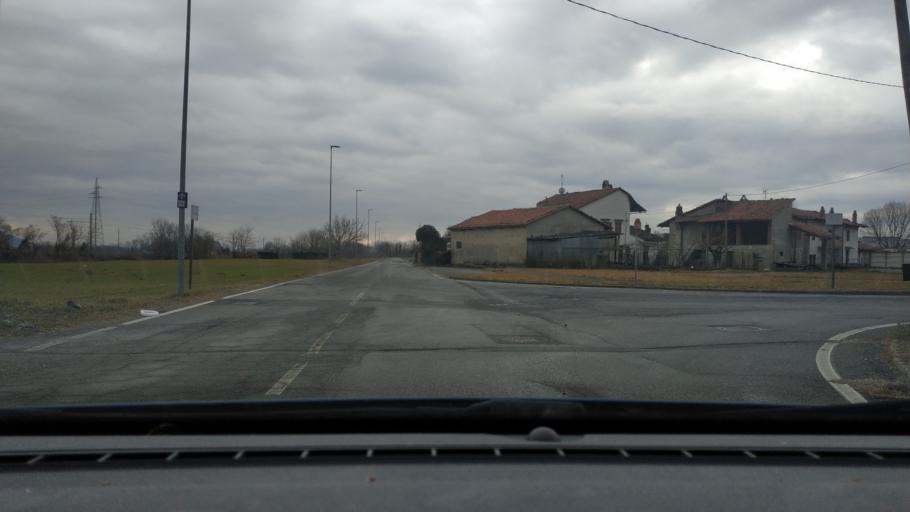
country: IT
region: Piedmont
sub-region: Provincia di Torino
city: Ivrea
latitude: 45.4348
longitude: 7.8898
